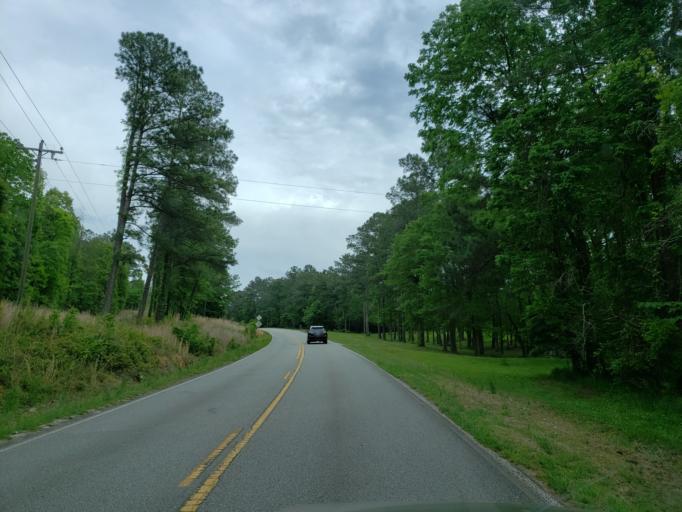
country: US
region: Georgia
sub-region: Bibb County
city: West Point
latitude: 32.8166
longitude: -83.8568
